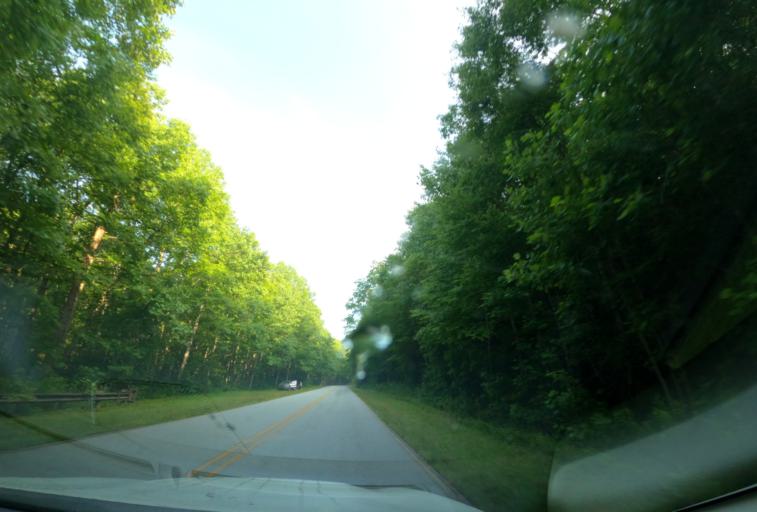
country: US
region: North Carolina
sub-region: Transylvania County
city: Brevard
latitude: 35.2562
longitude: -82.9021
